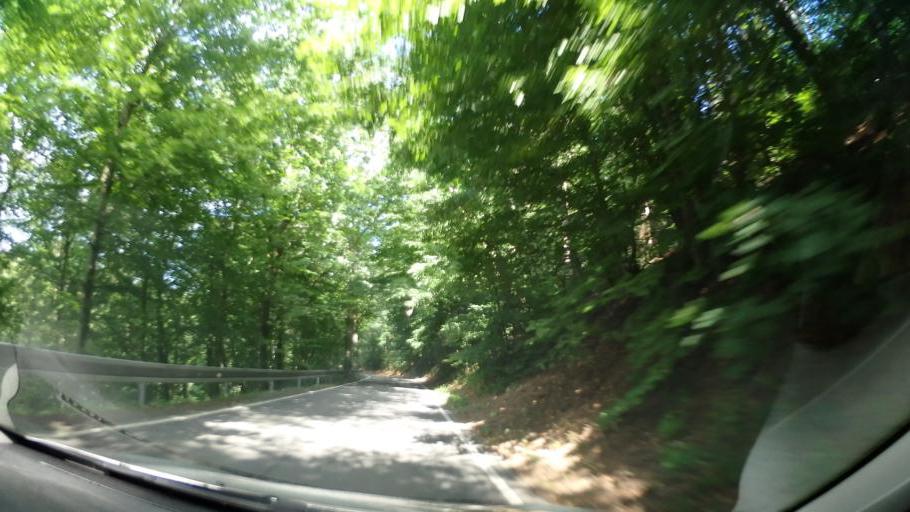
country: CZ
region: Olomoucky
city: Zabreh
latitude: 49.8675
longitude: 16.8371
